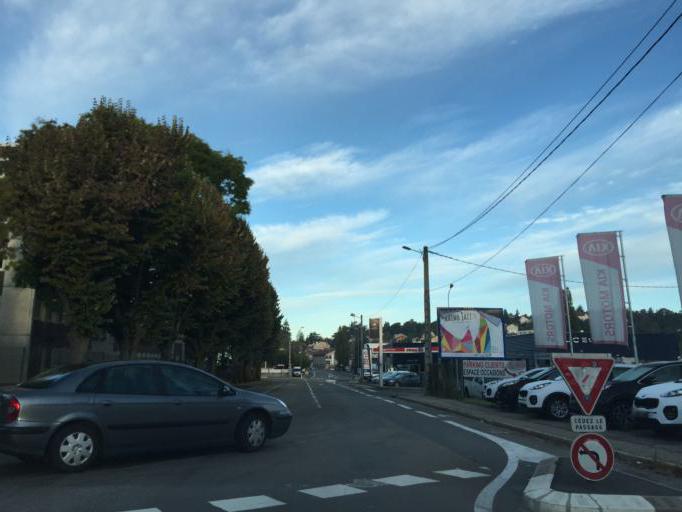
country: FR
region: Rhone-Alpes
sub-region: Departement de la Loire
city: Saint-Priest-en-Jarez
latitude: 45.4669
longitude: 4.3856
